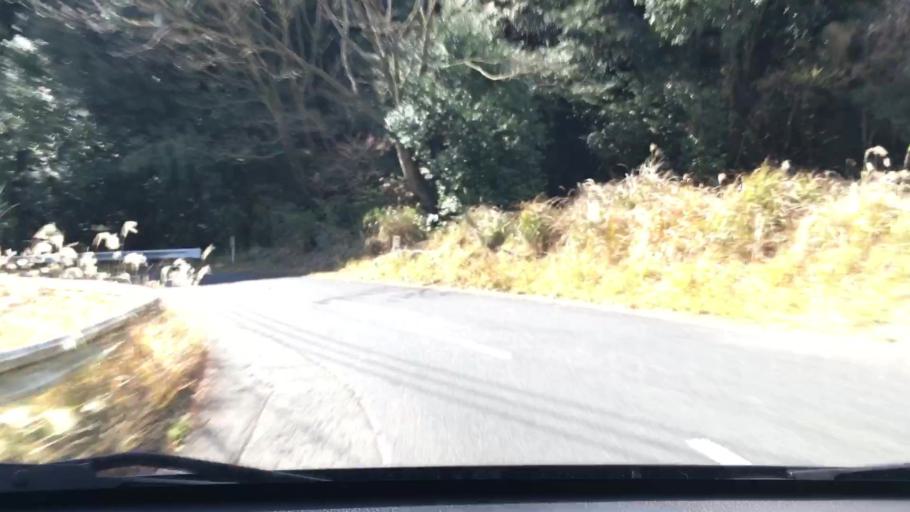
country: JP
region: Kagoshima
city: Ijuin
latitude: 31.7126
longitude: 130.4232
